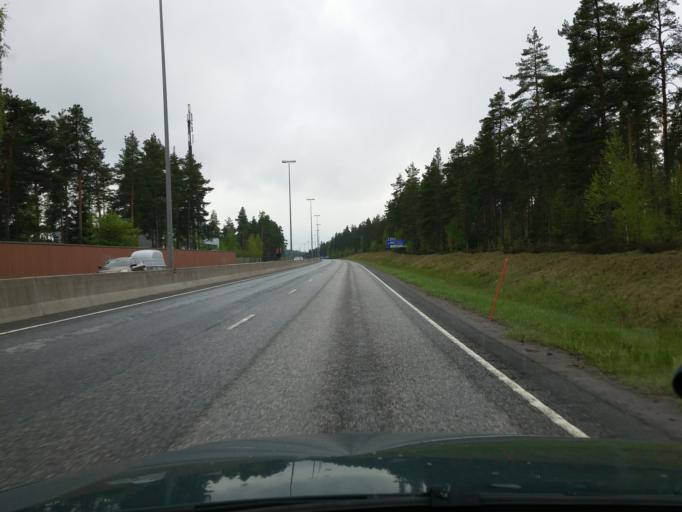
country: FI
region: Uusimaa
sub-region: Helsinki
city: Lohja
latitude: 60.2675
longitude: 24.1125
